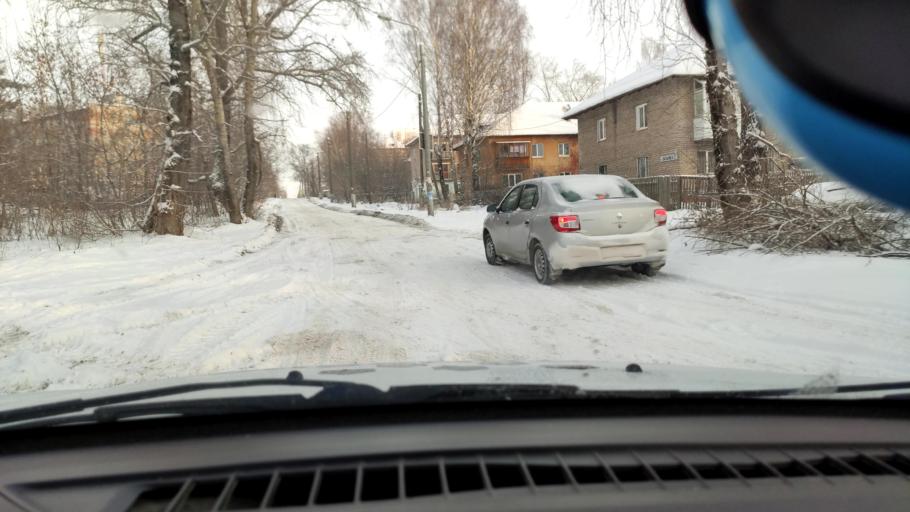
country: RU
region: Perm
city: Perm
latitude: 58.0971
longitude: 56.2898
